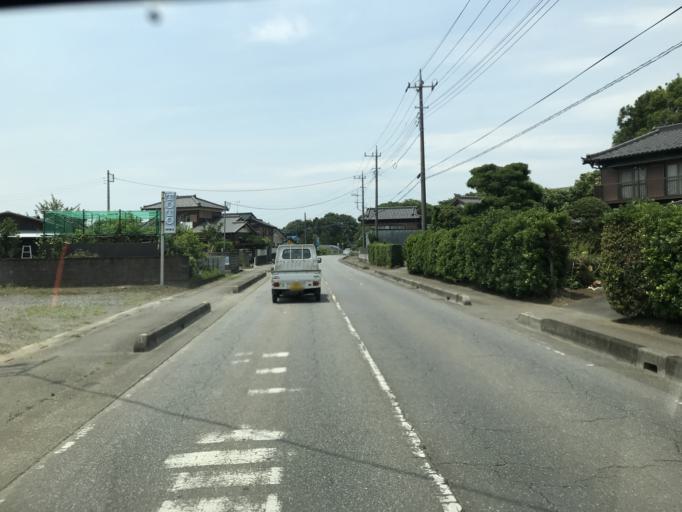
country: JP
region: Ibaraki
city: Sakai
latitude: 36.0377
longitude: 139.8100
